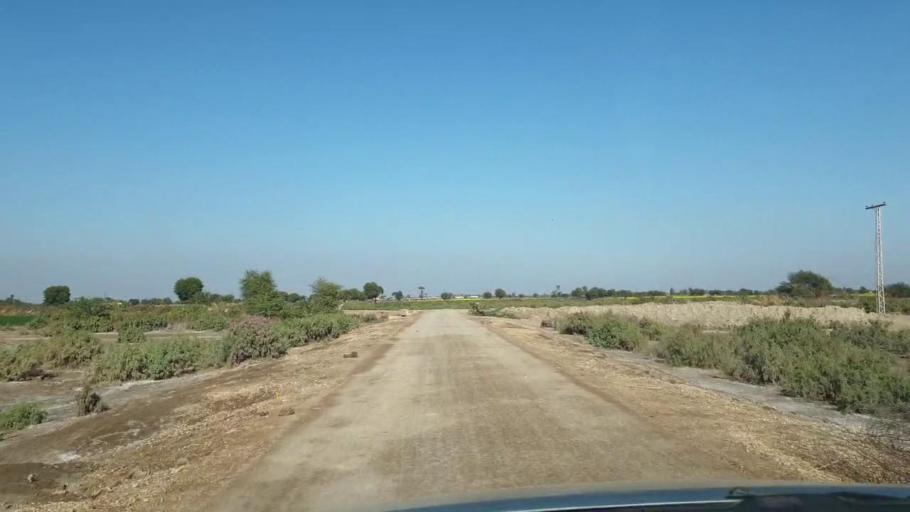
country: PK
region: Sindh
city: Jhol
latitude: 25.9196
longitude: 68.9862
